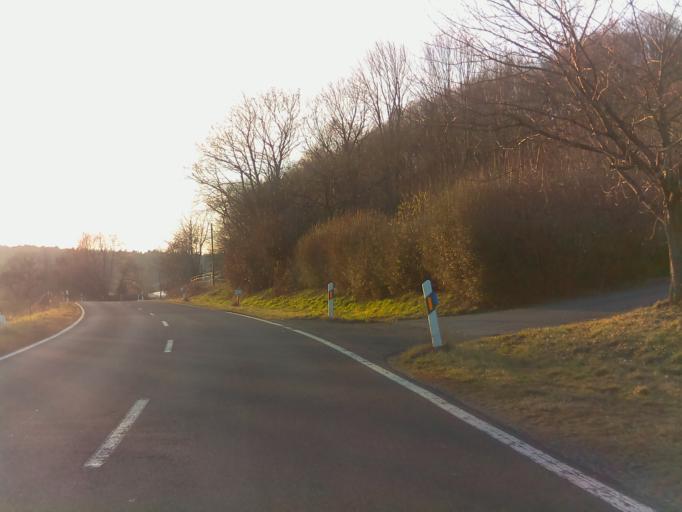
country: DE
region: Bavaria
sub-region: Regierungsbezirk Unterfranken
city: Geiselbach
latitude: 50.1280
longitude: 9.2072
